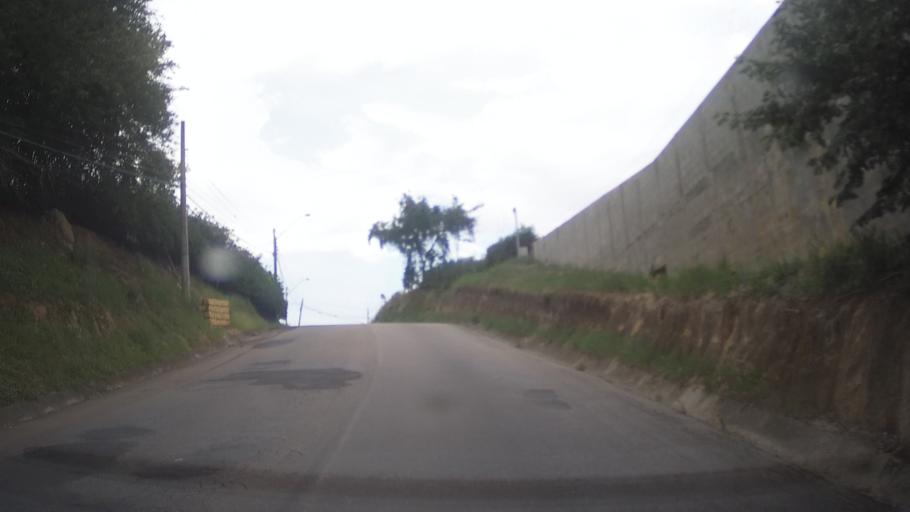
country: BR
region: Sao Paulo
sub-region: Itupeva
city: Itupeva
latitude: -23.1728
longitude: -47.1101
